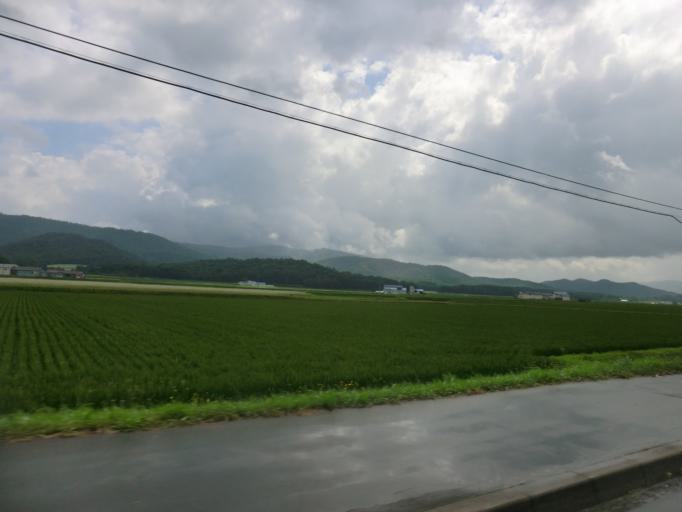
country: JP
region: Hokkaido
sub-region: Asahikawa-shi
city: Asahikawa
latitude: 44.0360
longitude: 142.1496
